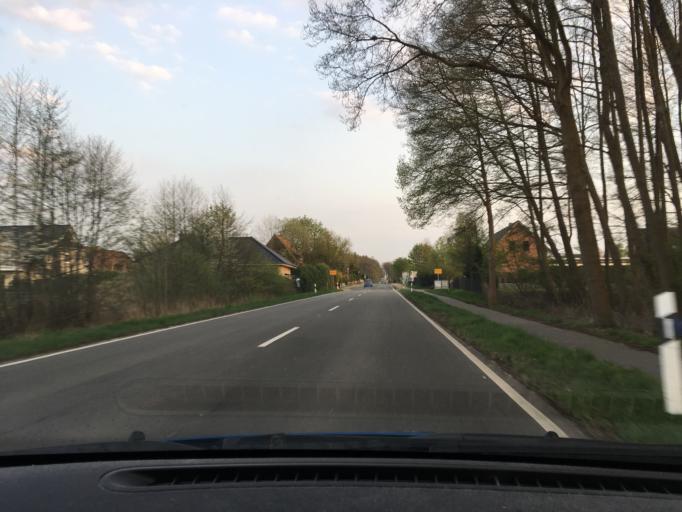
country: DE
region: Lower Saxony
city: Amelinghausen
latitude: 53.1379
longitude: 10.2133
